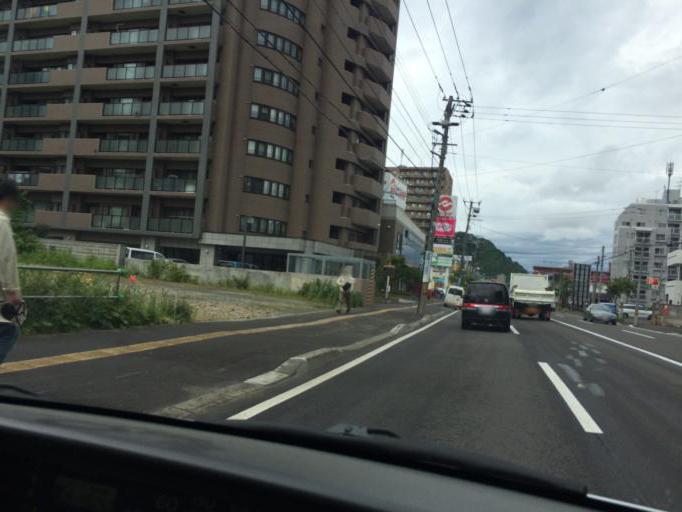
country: JP
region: Hokkaido
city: Sapporo
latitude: 43.0347
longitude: 141.3340
